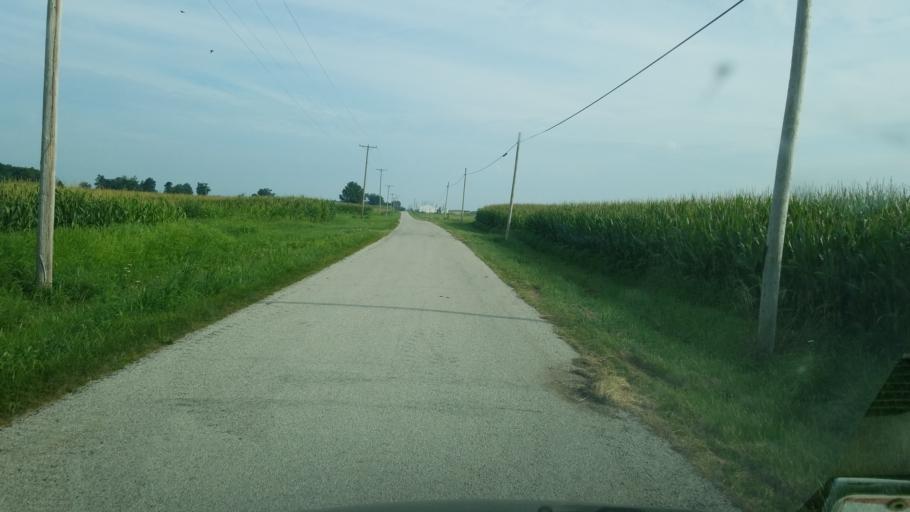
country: US
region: Ohio
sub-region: Crawford County
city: Bucyrus
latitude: 40.7493
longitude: -82.9379
